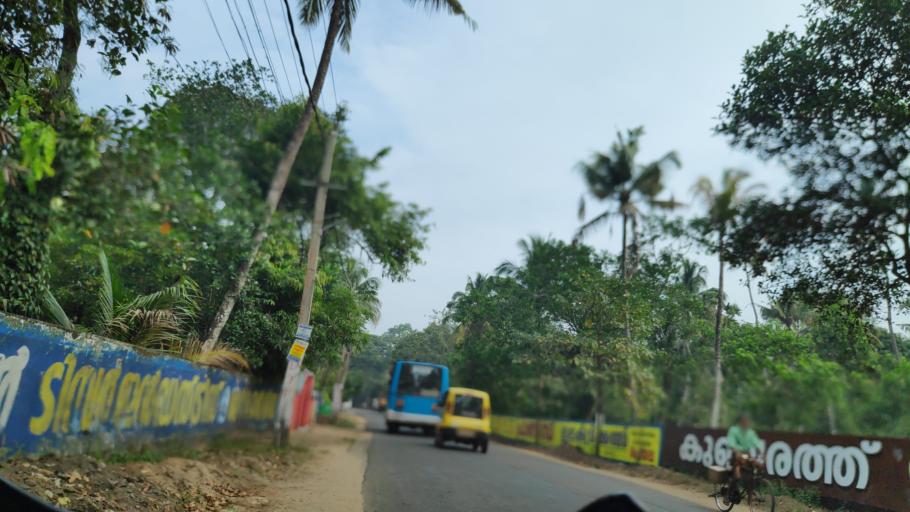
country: IN
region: Kerala
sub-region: Alappuzha
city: Shertallai
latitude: 9.7038
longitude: 76.3566
